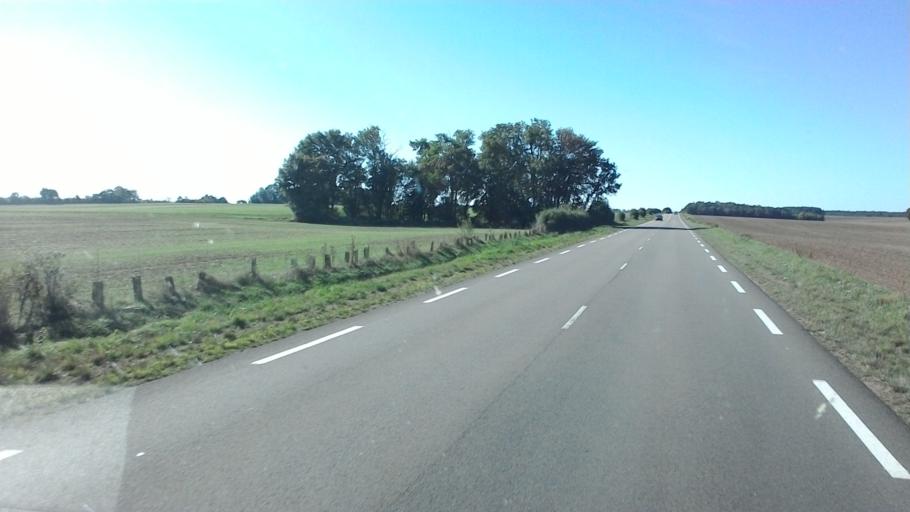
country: FR
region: Bourgogne
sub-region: Departement de la Cote-d'Or
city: Chatillon-sur-Seine
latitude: 47.8465
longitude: 4.5543
